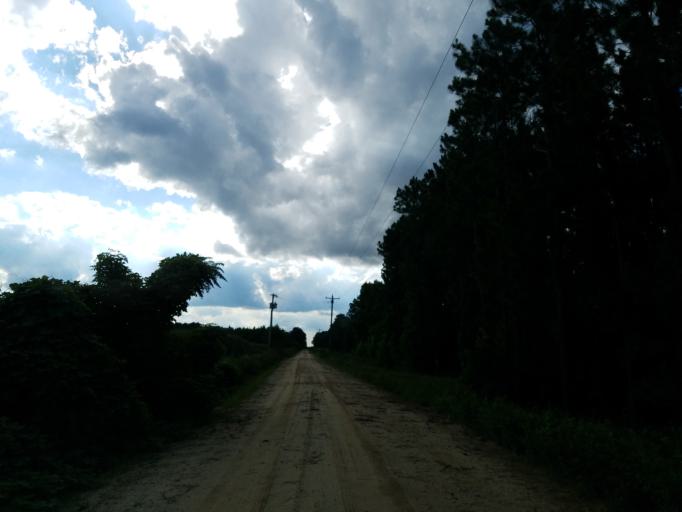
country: US
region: Georgia
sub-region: Turner County
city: Ashburn
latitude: 31.7445
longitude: -83.6616
